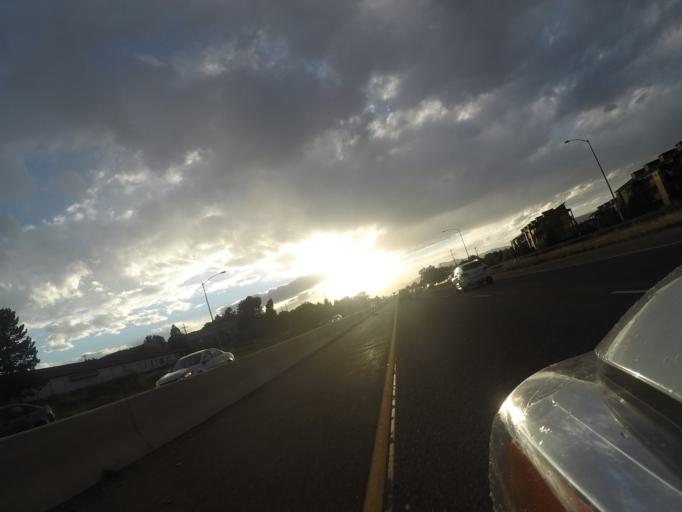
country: US
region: Colorado
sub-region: Arapahoe County
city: Sheridan
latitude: 39.6533
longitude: -105.0558
